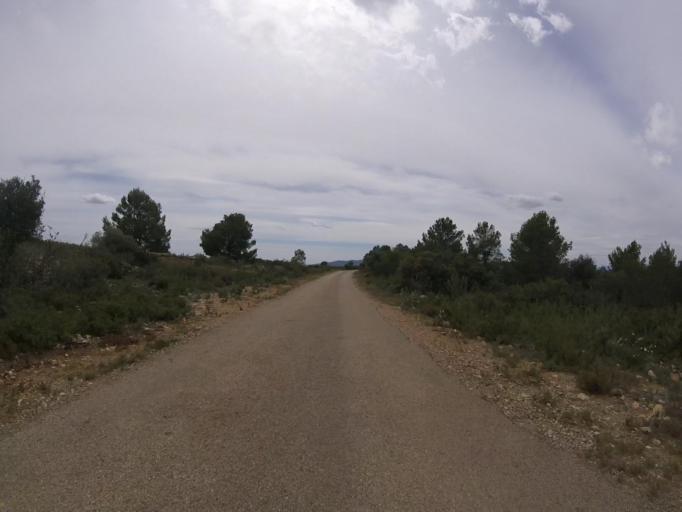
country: ES
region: Valencia
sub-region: Provincia de Castello
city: Sierra-Engarceran
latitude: 40.2264
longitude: -0.0225
